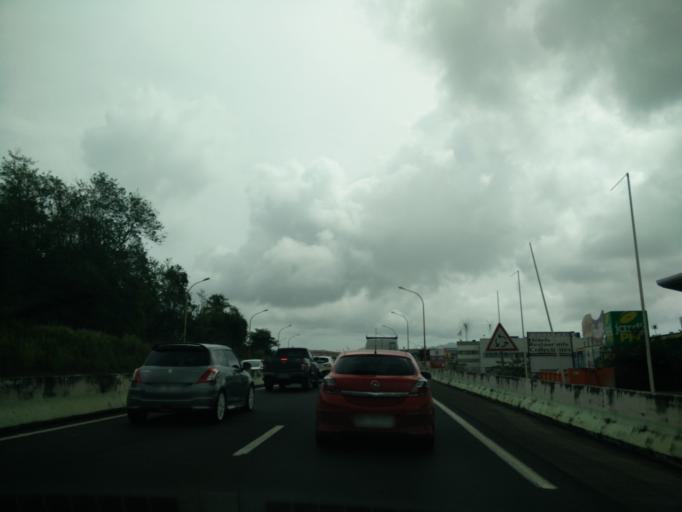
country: MQ
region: Martinique
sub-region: Martinique
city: Ducos
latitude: 14.5783
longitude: -60.9837
